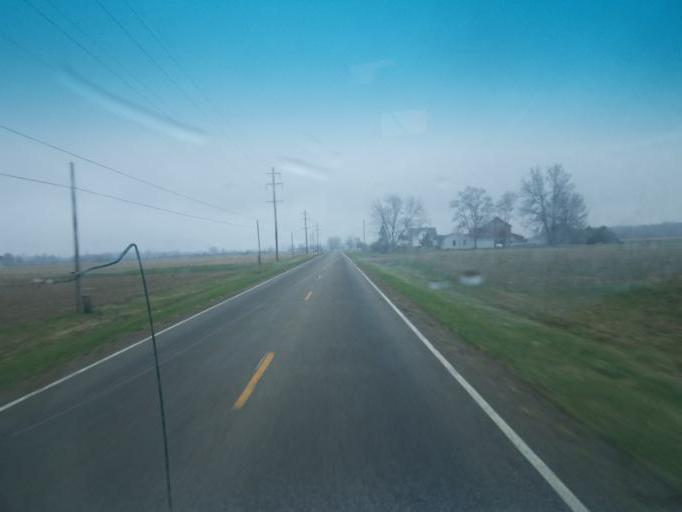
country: US
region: Ohio
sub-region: Defiance County
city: Hicksville
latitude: 41.3434
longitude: -84.7670
